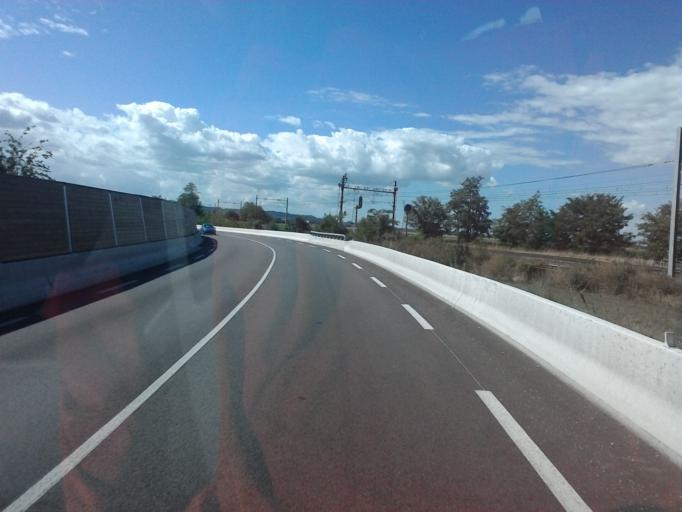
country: FR
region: Rhone-Alpes
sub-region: Departement de l'Ain
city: Ambronay
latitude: 45.9942
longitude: 5.3406
